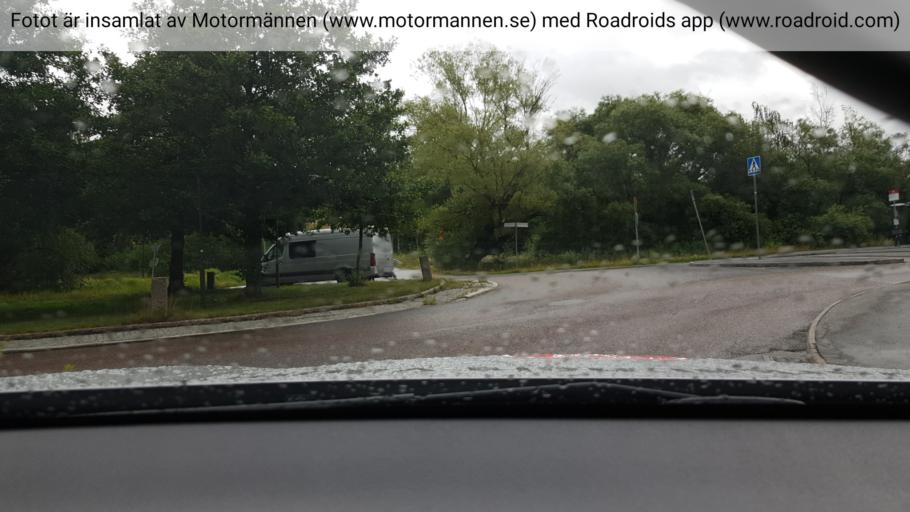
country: SE
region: Stockholm
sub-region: Huddinge Kommun
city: Huddinge
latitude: 59.2412
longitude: 17.9782
